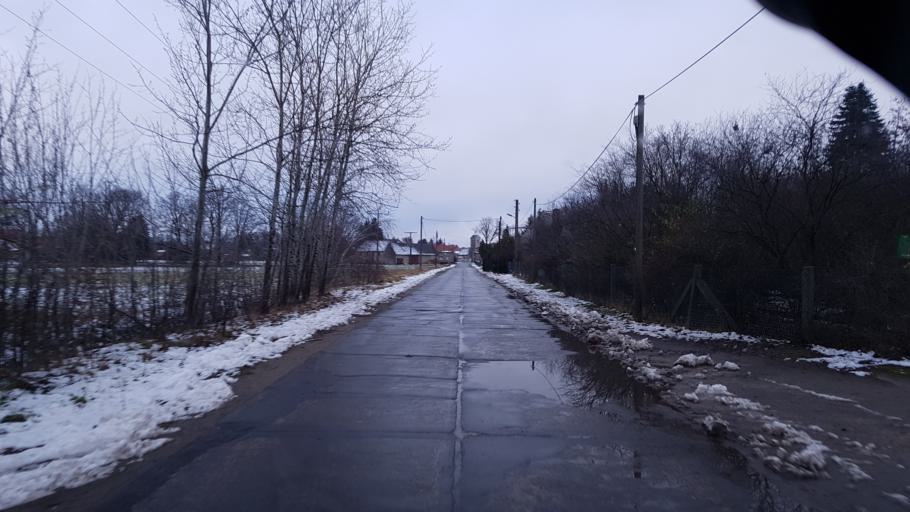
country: DE
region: Brandenburg
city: Luckau
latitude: 51.8152
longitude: 13.6978
